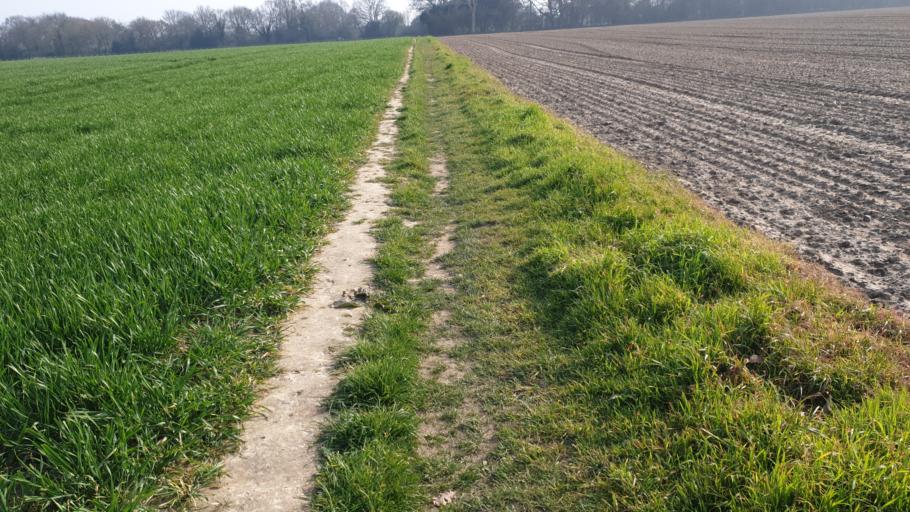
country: GB
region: England
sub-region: Essex
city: Little Clacton
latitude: 51.8787
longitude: 1.1181
